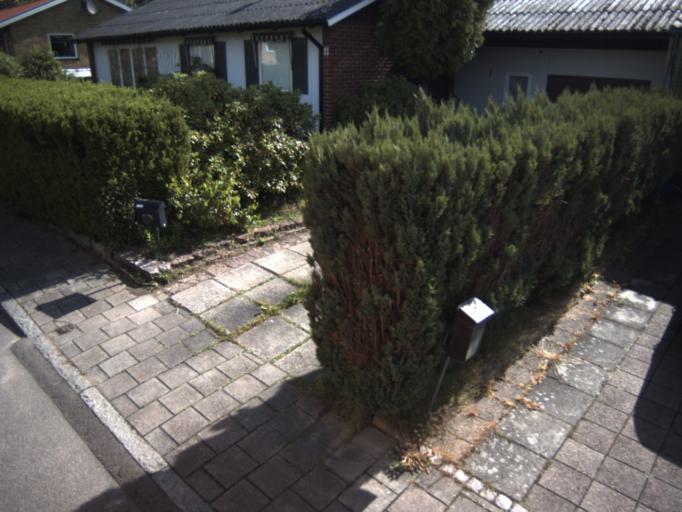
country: SE
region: Skane
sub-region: Helsingborg
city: Helsingborg
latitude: 56.0288
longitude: 12.7379
